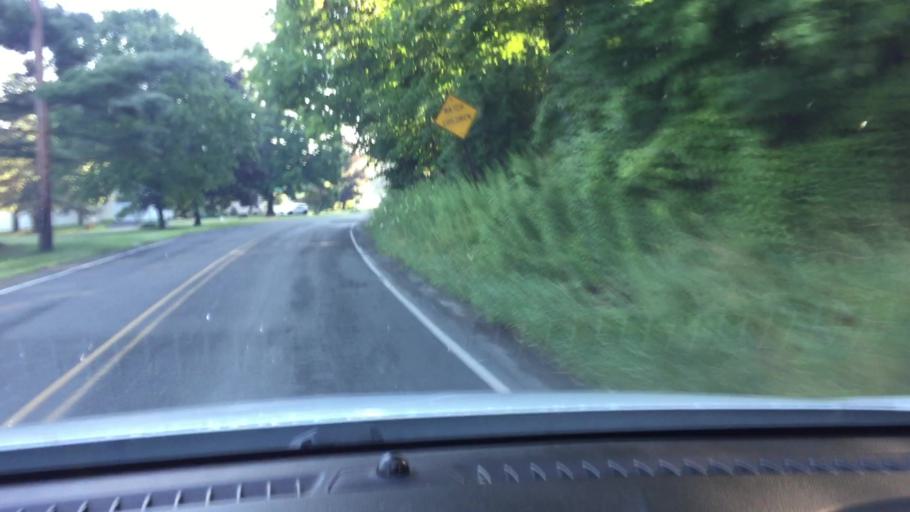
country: US
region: Massachusetts
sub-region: Berkshire County
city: Pittsfield
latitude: 42.4144
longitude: -73.2303
